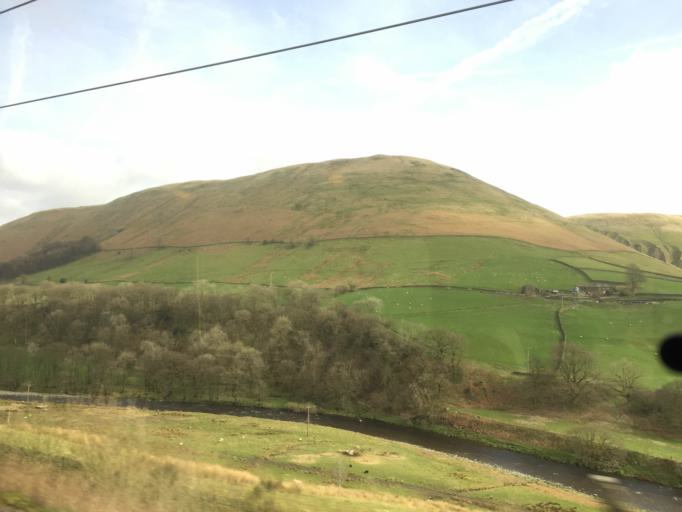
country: GB
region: England
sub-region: Cumbria
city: Sedbergh
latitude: 54.3881
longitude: -2.5873
